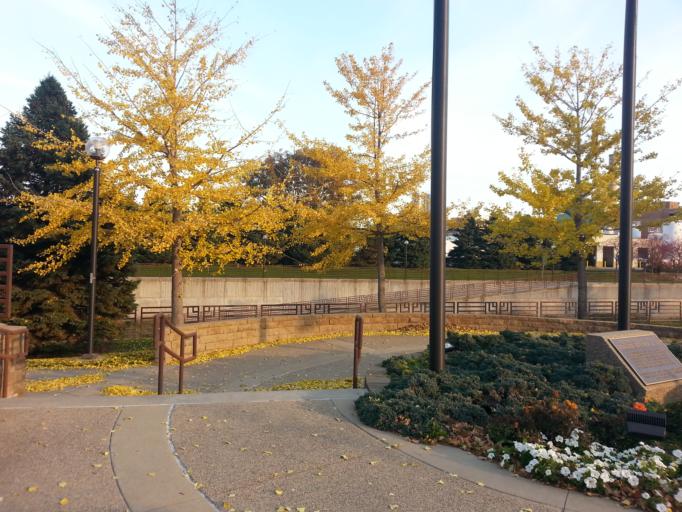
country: US
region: Minnesota
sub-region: Olmsted County
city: Rochester
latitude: 44.0174
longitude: -92.4629
